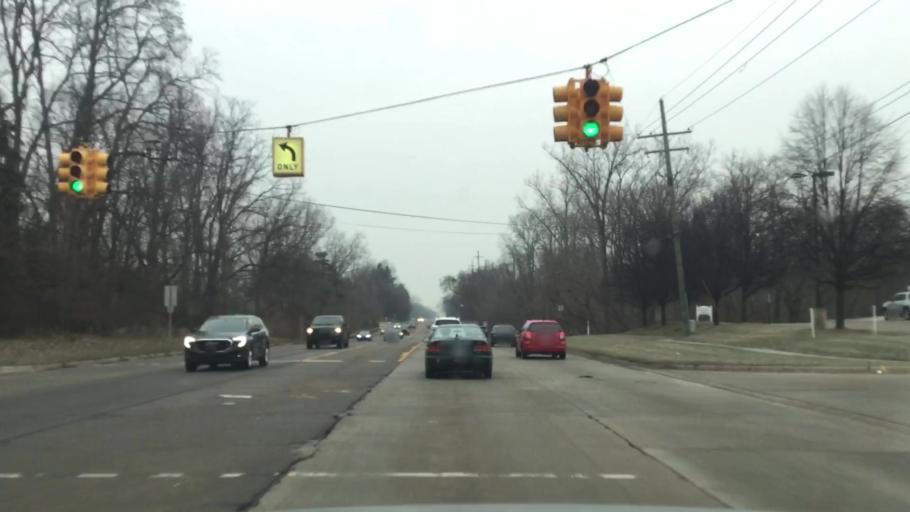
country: US
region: Michigan
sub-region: Oakland County
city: Farmington
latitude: 42.4190
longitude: -83.3550
